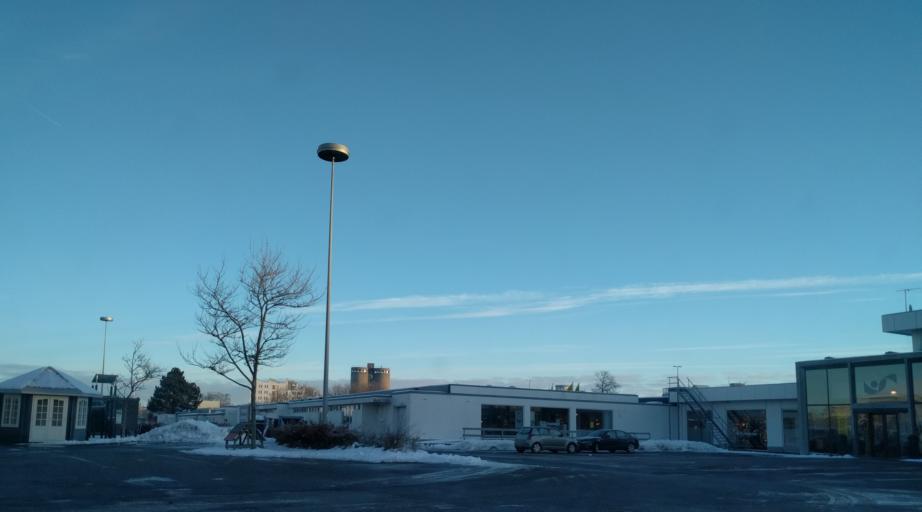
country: DK
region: North Denmark
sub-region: Alborg Kommune
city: Aalborg
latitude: 57.0333
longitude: 9.9285
